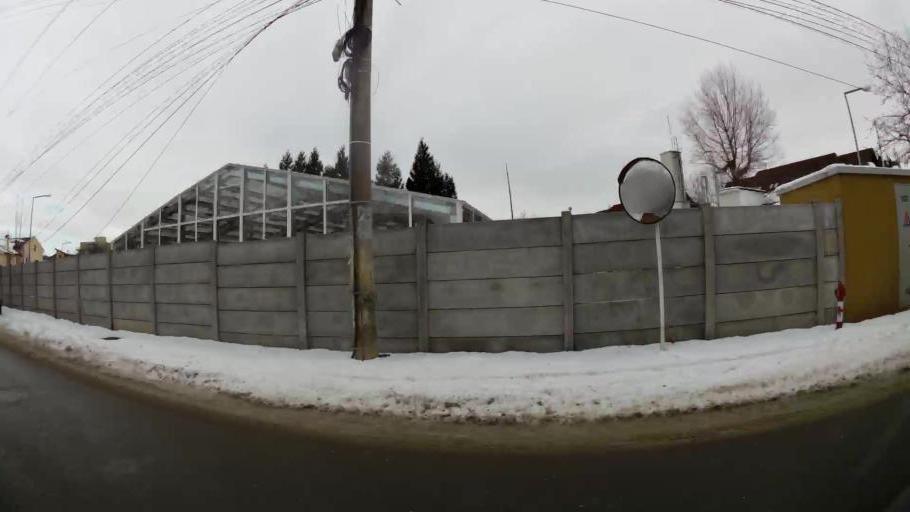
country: RO
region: Ilfov
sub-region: Comuna Otopeni
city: Otopeni
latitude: 44.5131
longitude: 26.1060
